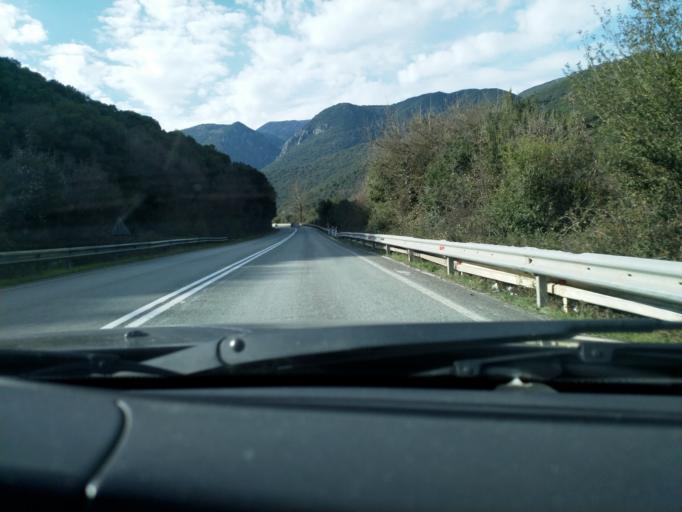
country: GR
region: Epirus
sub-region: Nomos Ioanninon
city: Agia Kyriaki
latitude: 39.4404
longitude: 20.8526
